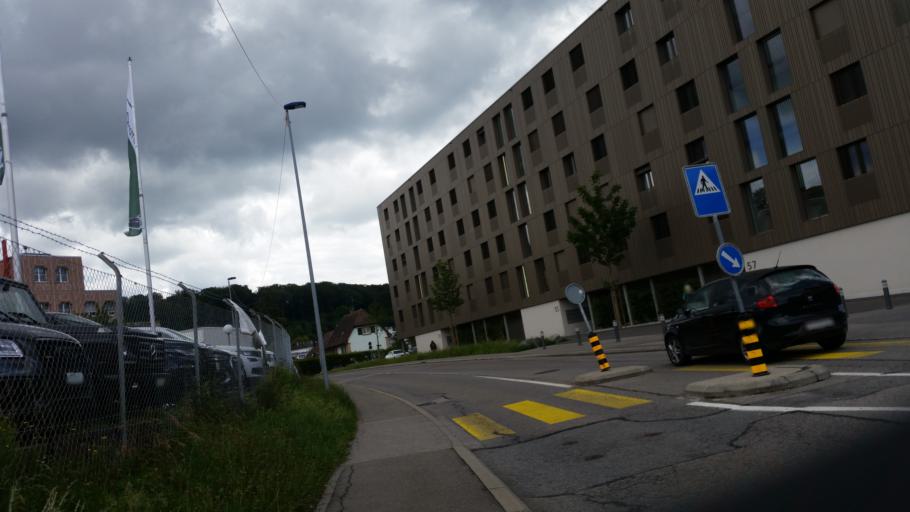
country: CH
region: Vaud
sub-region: Lausanne District
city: Blecherette
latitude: 46.5419
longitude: 6.6284
